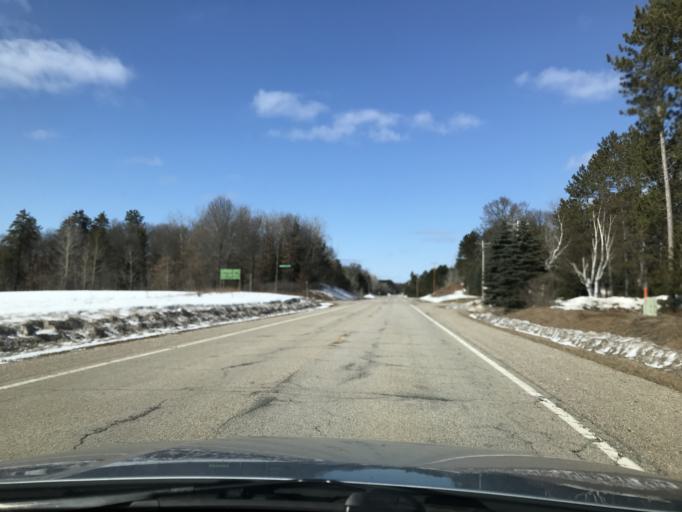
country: US
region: Wisconsin
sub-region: Marinette County
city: Peshtigo
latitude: 45.3248
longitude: -88.1020
